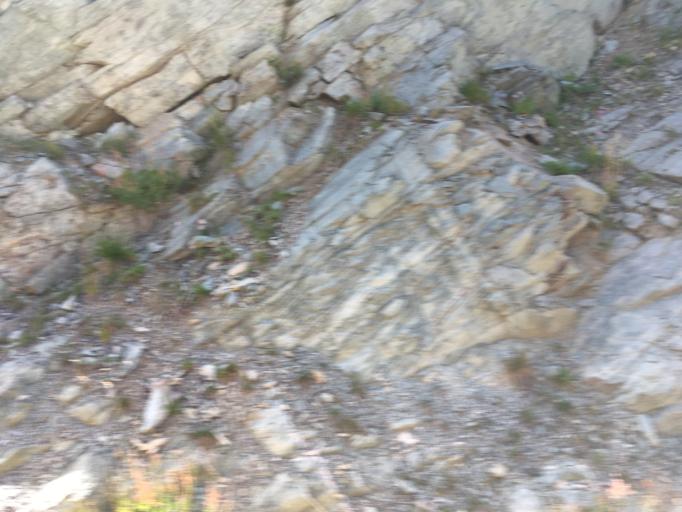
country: CH
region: Grisons
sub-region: Maloja District
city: Silvaplana
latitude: 46.4661
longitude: 9.6908
